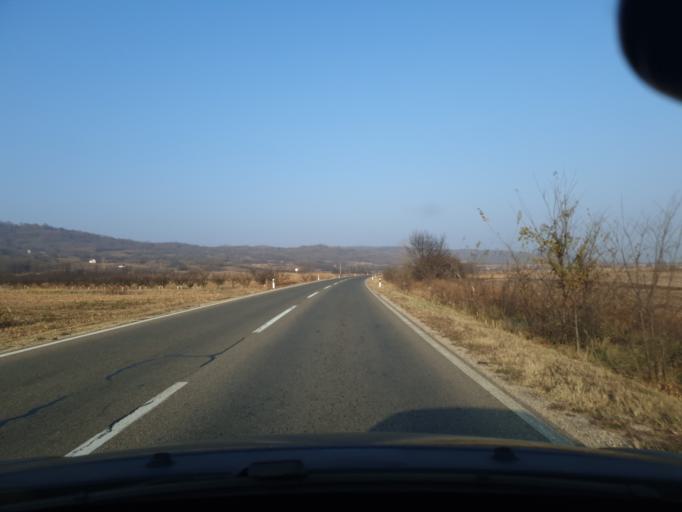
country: RS
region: Central Serbia
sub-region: Jablanicki Okrug
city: Leskovac
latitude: 42.9397
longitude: 21.9994
